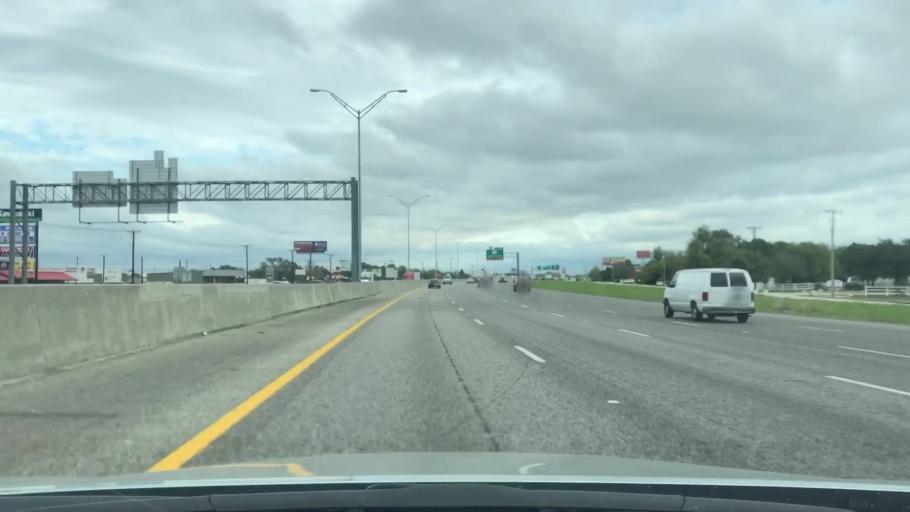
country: US
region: Texas
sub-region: Comal County
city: New Braunfels
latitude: 29.7180
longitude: -98.0878
